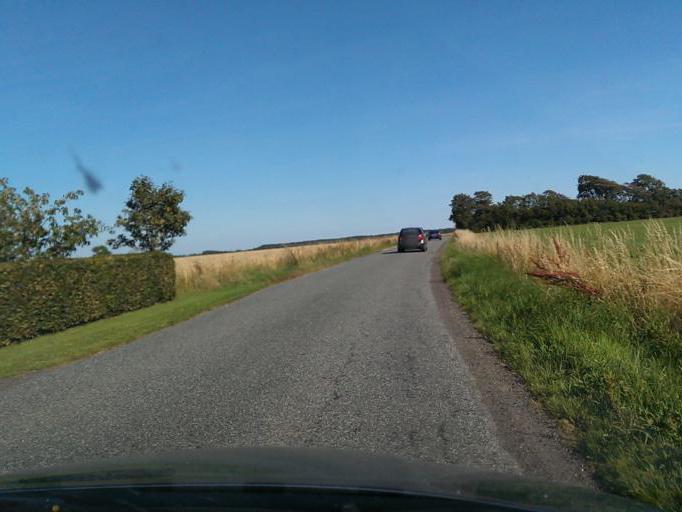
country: DK
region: Central Jutland
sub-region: Odder Kommune
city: Odder
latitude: 55.8632
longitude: 10.1101
